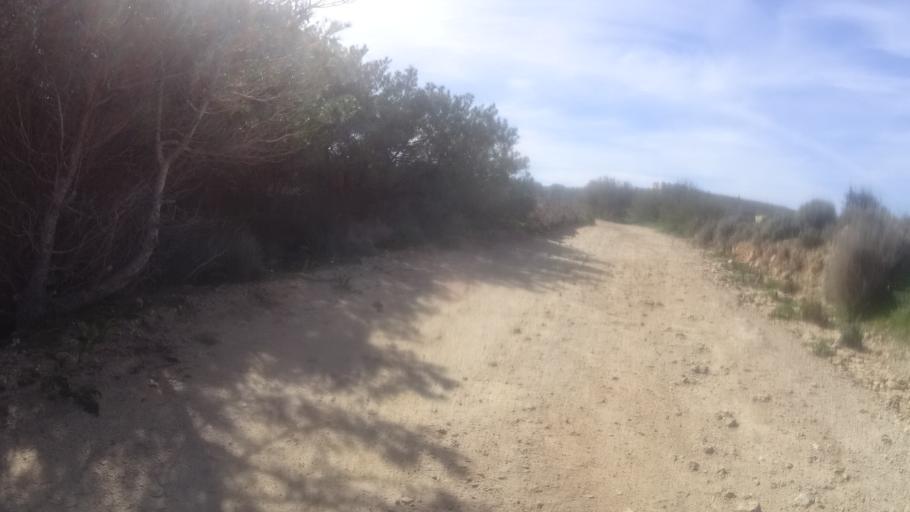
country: MT
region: Il-Qala
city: Qala
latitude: 36.0136
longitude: 14.3339
